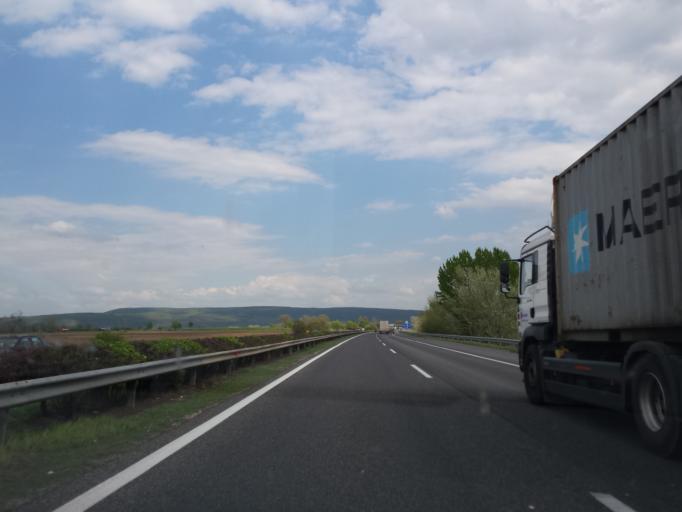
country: HU
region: Komarom-Esztergom
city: Tata
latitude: 47.6253
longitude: 18.3059
